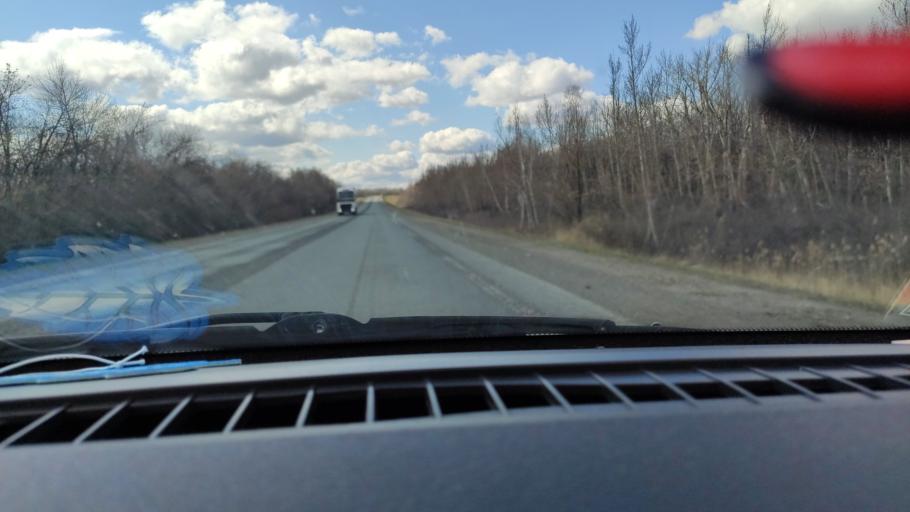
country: RU
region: Saratov
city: Dukhovnitskoye
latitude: 52.6256
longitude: 48.1793
